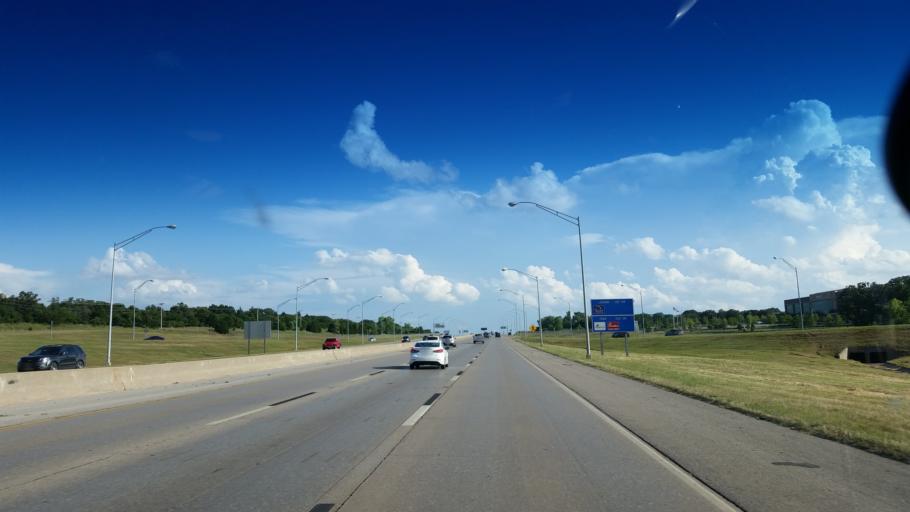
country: US
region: Oklahoma
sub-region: Oklahoma County
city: Edmond
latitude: 35.6381
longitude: -97.4250
